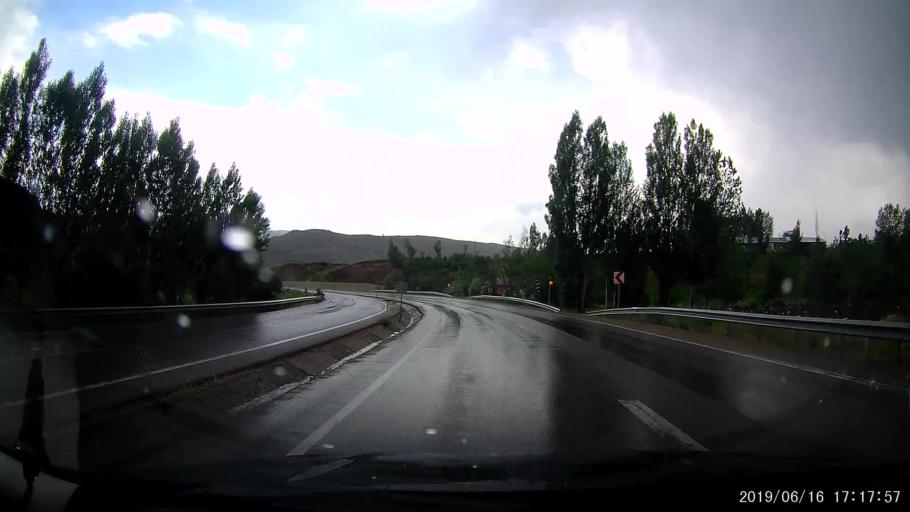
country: TR
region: Erzincan
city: Tercan
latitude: 39.8206
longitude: 40.5294
